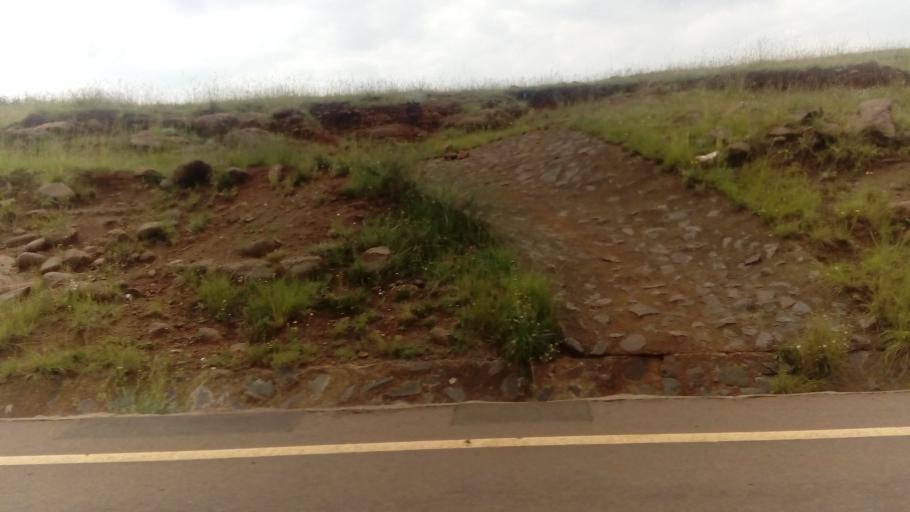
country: LS
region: Leribe
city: Leribe
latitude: -29.0374
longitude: 28.2484
